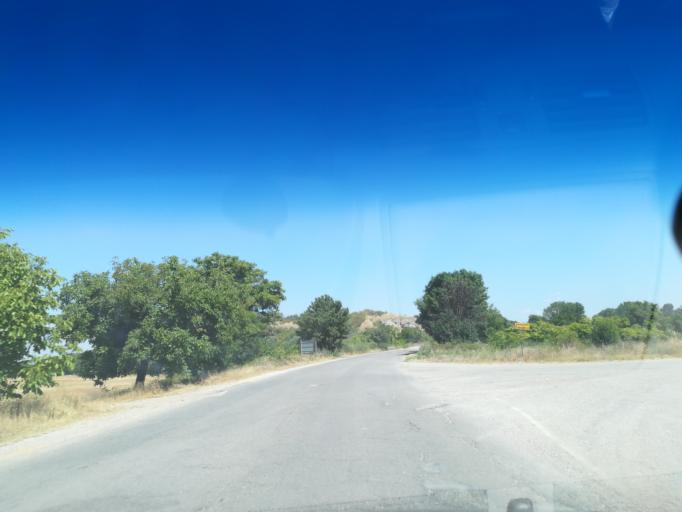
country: BG
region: Plovdiv
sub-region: Obshtina Sadovo
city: Sadovo
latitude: 42.0264
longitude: 24.9851
